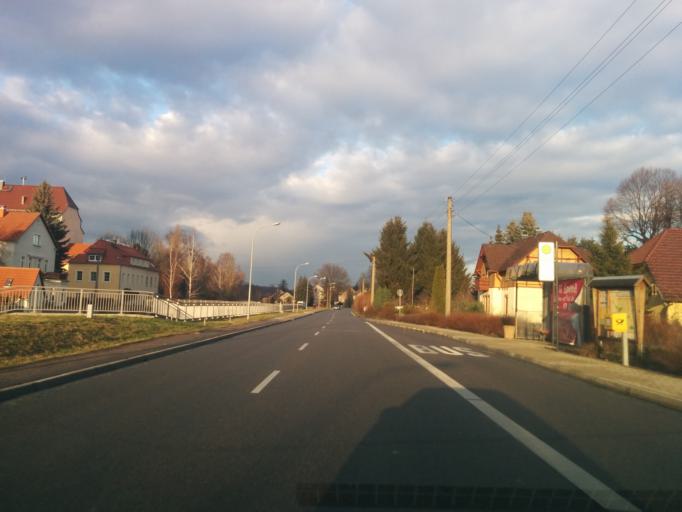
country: DE
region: Saxony
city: Frankenberg
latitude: 50.9033
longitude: 13.0172
